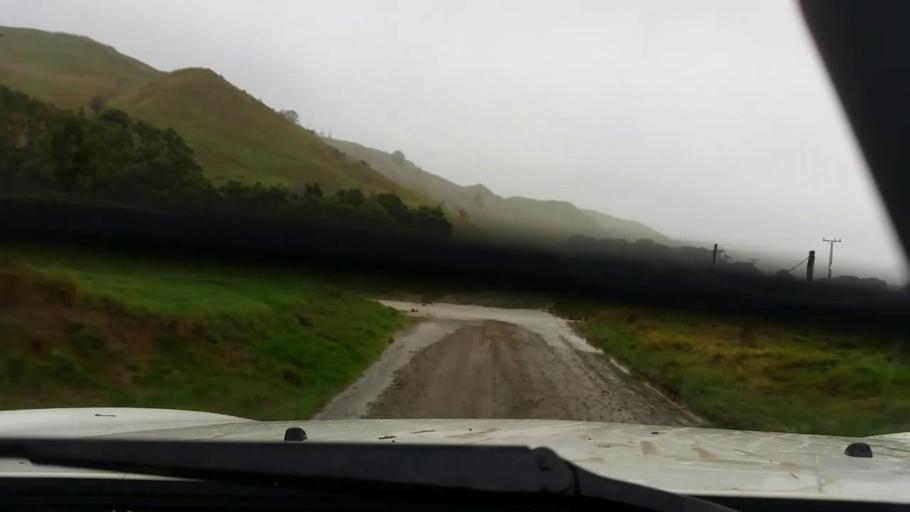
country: NZ
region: Wellington
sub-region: Masterton District
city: Masterton
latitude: -41.2613
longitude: 175.8960
